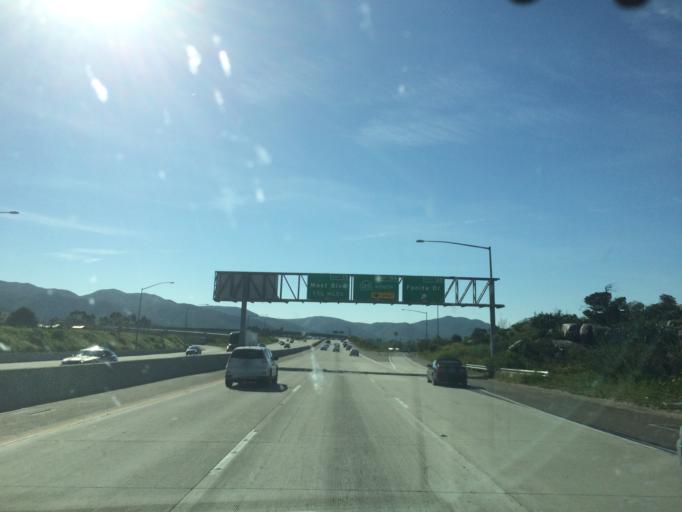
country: US
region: California
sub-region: San Diego County
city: Santee
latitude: 32.8368
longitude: -116.9955
